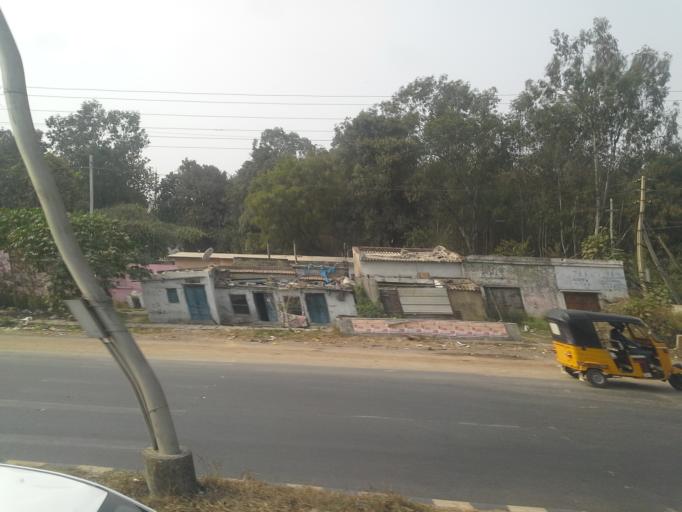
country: IN
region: Telangana
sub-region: Medak
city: Patancheru
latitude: 17.5222
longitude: 78.2748
